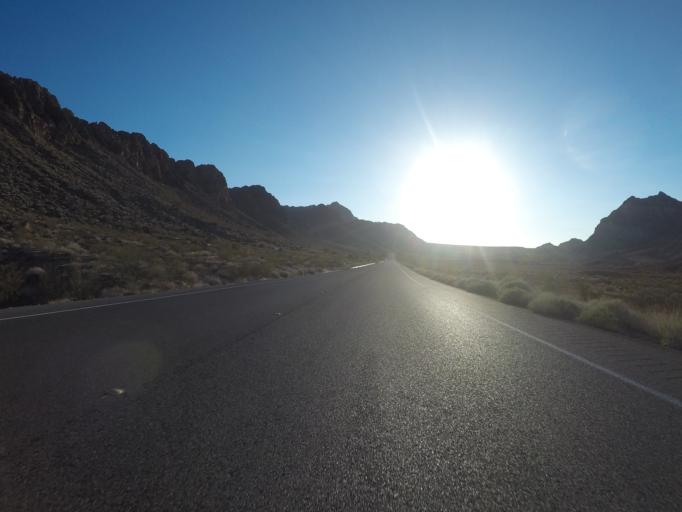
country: US
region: Nevada
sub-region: Clark County
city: Moapa Valley
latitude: 36.2518
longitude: -114.4840
